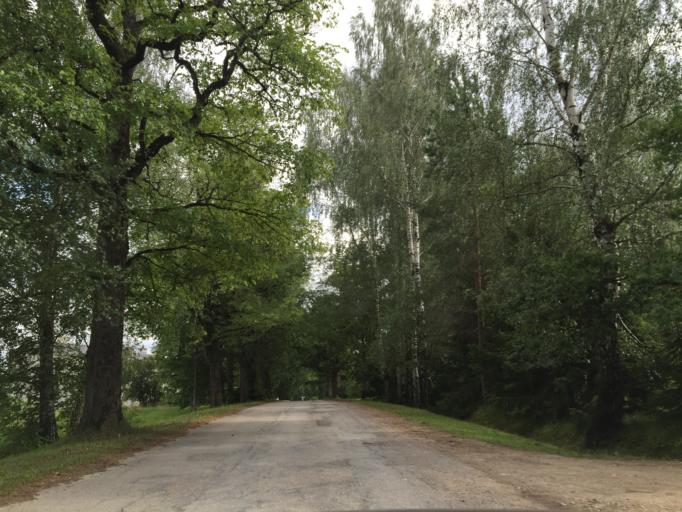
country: LV
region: Malpils
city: Malpils
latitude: 56.8600
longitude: 25.0188
